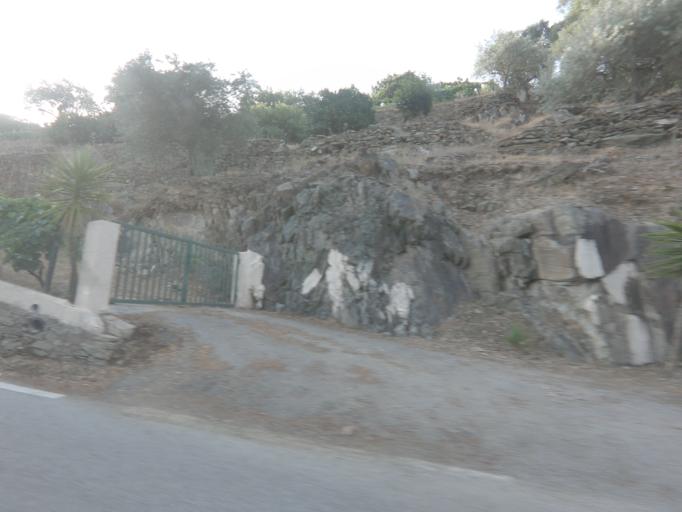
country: PT
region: Vila Real
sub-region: Sabrosa
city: Vilela
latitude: 41.2024
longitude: -7.5366
